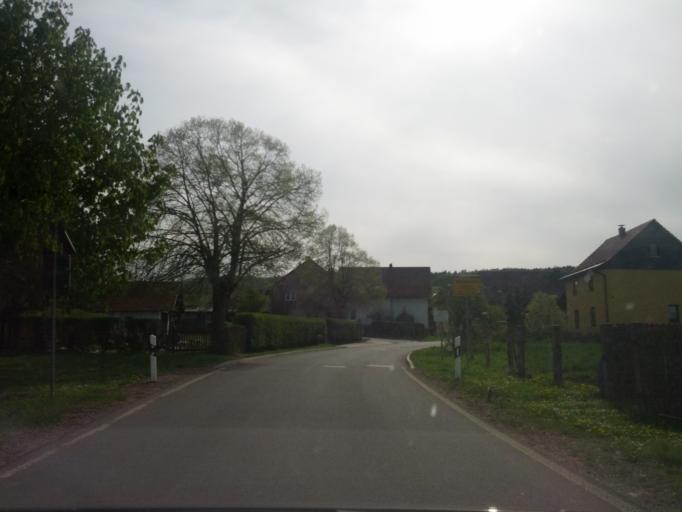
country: DE
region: Thuringia
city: Haina
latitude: 50.9638
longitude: 10.4812
